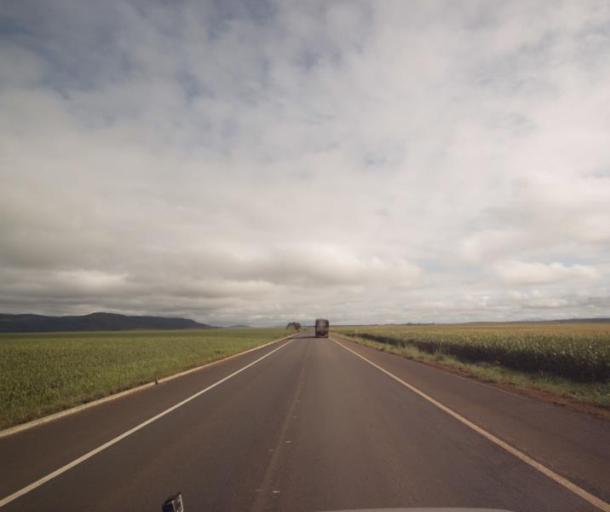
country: BR
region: Goias
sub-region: Padre Bernardo
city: Padre Bernardo
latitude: -15.4148
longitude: -48.6254
